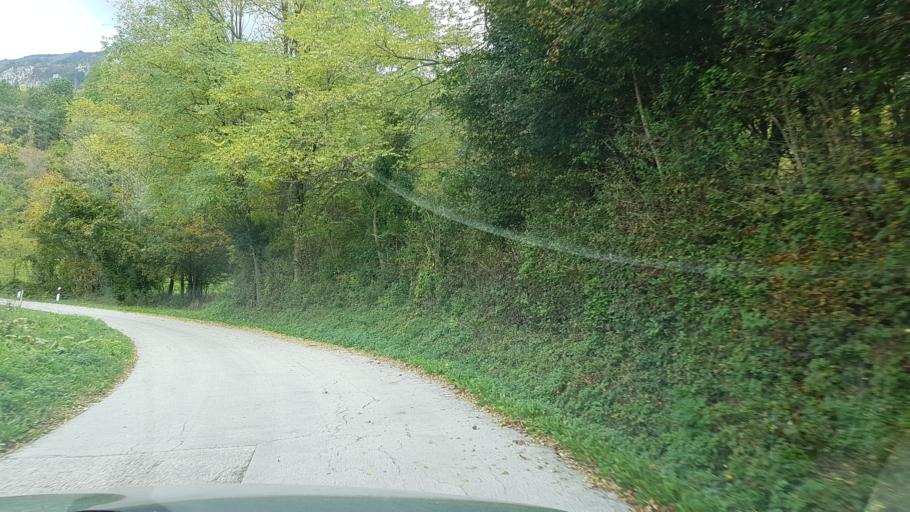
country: HR
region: Istarska
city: Buzet
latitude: 45.4065
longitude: 14.1195
